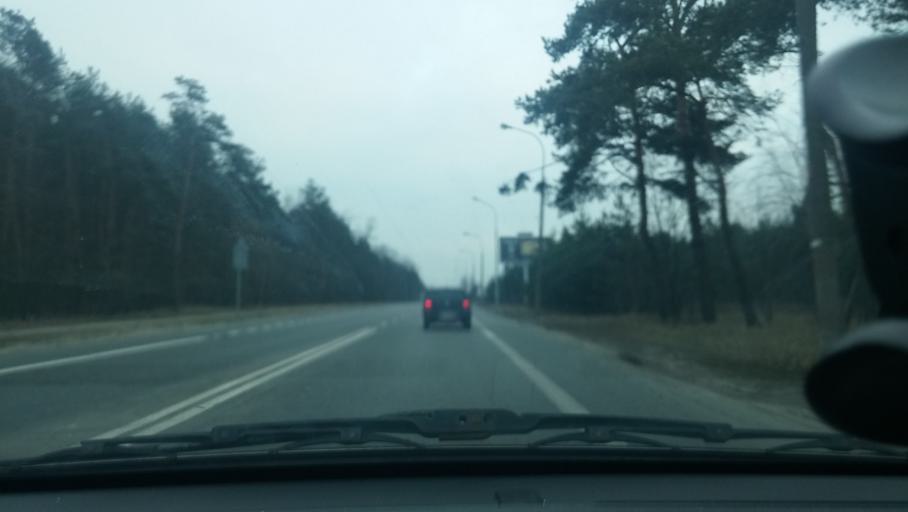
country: PL
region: Masovian Voivodeship
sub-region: Warszawa
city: Wawer
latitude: 52.2007
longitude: 21.1727
